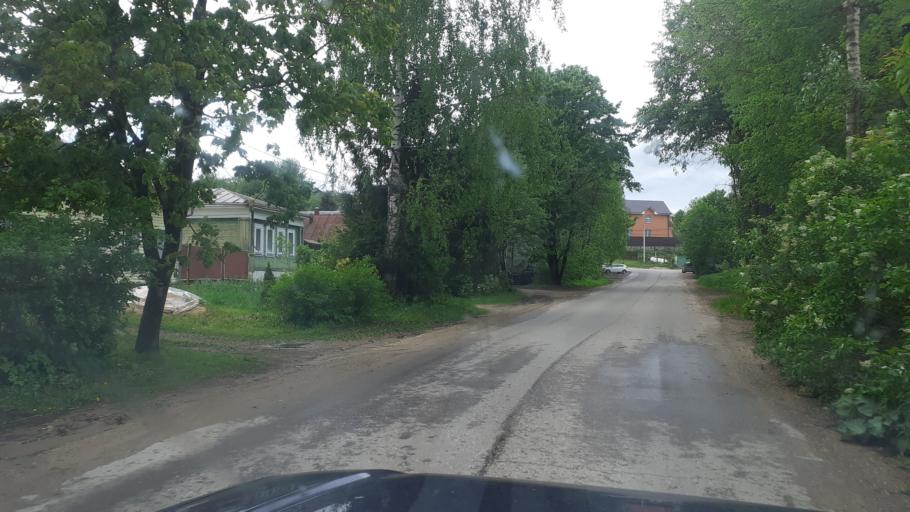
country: RU
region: Moskovskaya
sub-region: Volokolamskiy Rayon
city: Volokolamsk
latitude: 56.0363
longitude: 35.9526
